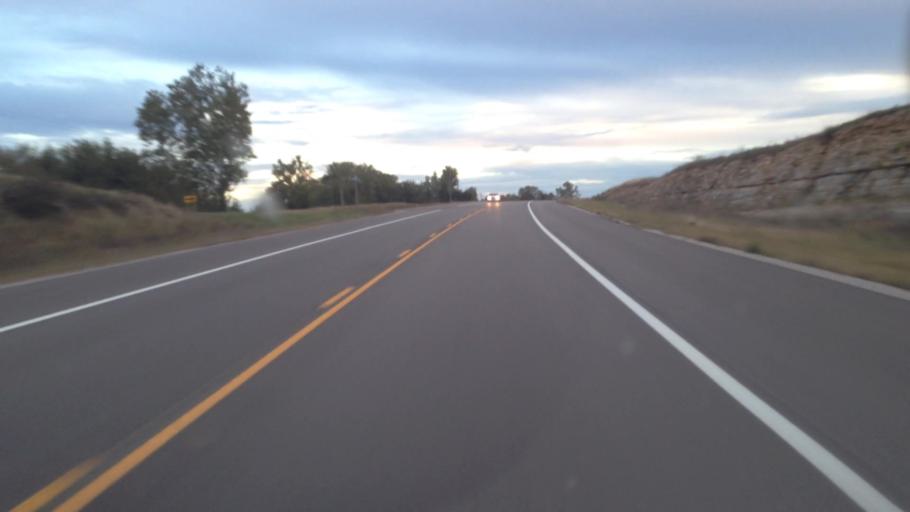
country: US
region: Kansas
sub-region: Anderson County
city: Garnett
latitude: 38.3320
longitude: -95.2490
